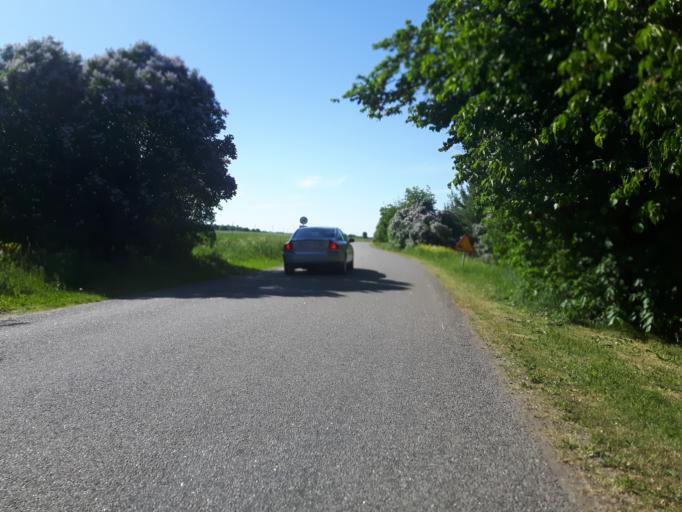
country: EE
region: Laeaene-Virumaa
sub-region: Haljala vald
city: Haljala
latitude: 59.5446
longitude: 26.1452
